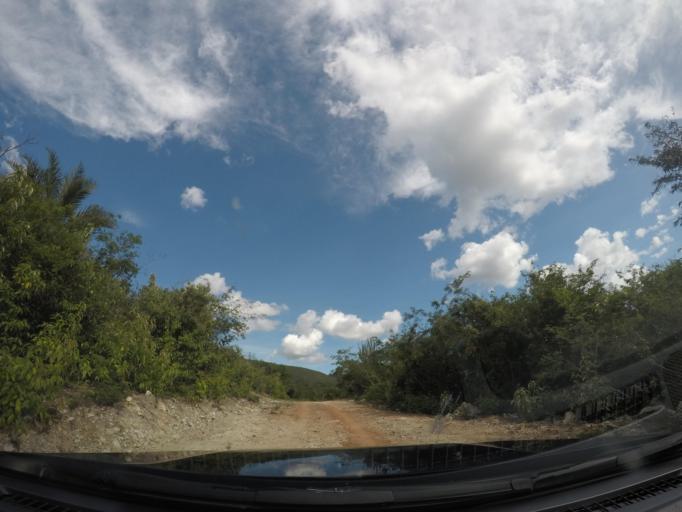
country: BR
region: Bahia
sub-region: Barra Da Estiva
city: Barra da Estiva
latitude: -13.1517
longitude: -41.5953
